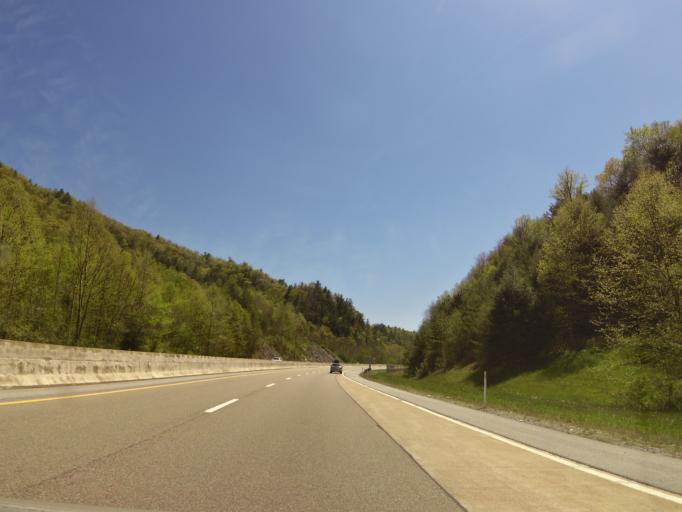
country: US
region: Tennessee
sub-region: Unicoi County
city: Banner Hill
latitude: 36.0827
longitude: -82.4949
